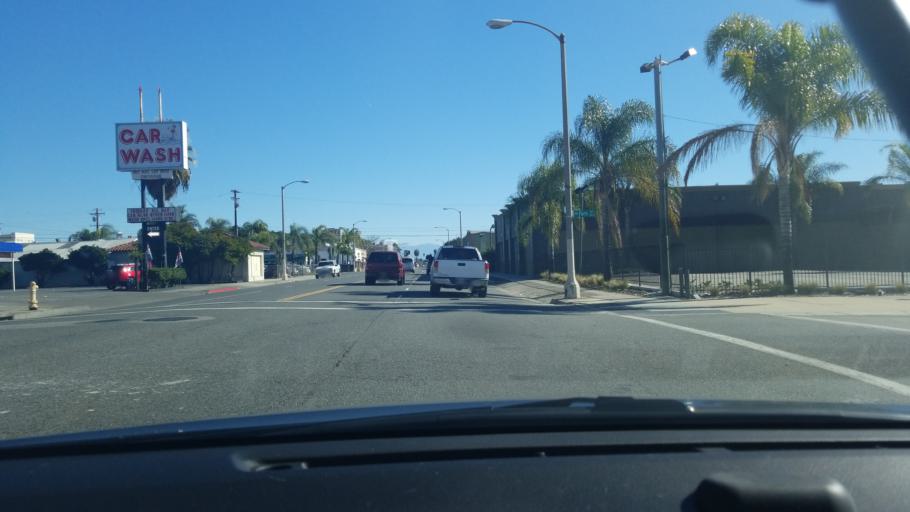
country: US
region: California
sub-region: San Bernardino County
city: Ontario
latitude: 34.0633
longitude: -117.6548
